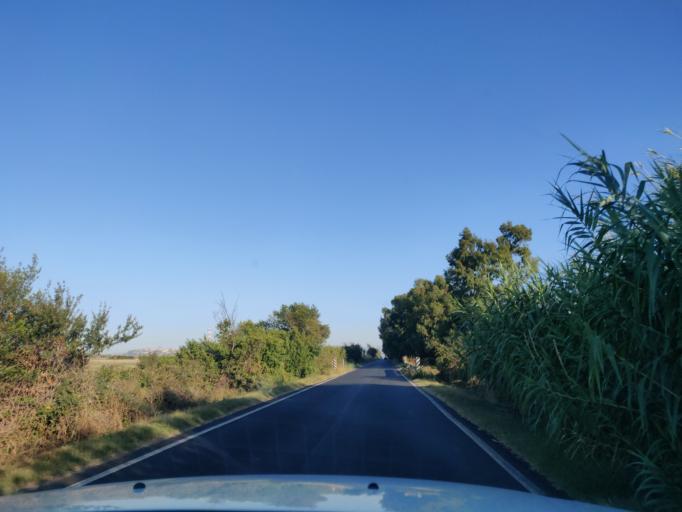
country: IT
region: Latium
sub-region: Provincia di Viterbo
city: Tarquinia
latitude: 42.2699
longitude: 11.6907
